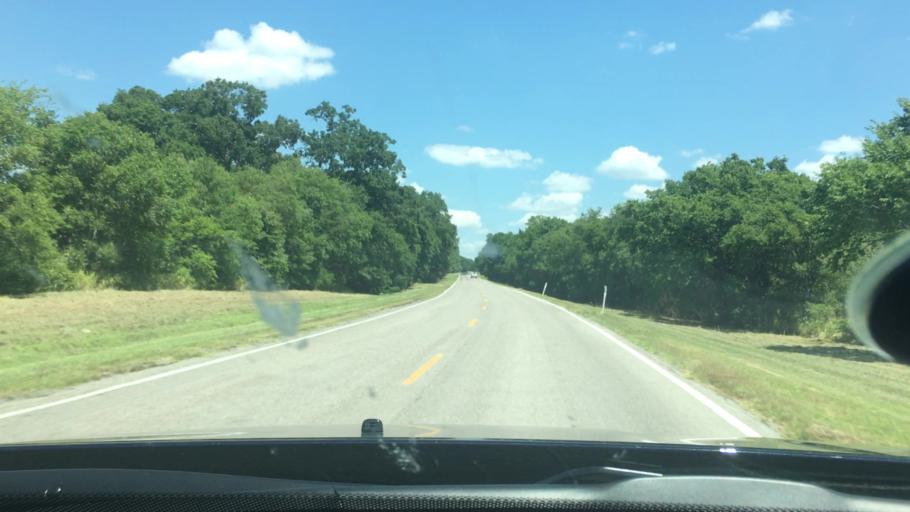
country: US
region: Oklahoma
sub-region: Carter County
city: Dickson
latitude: 34.3059
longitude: -96.9634
